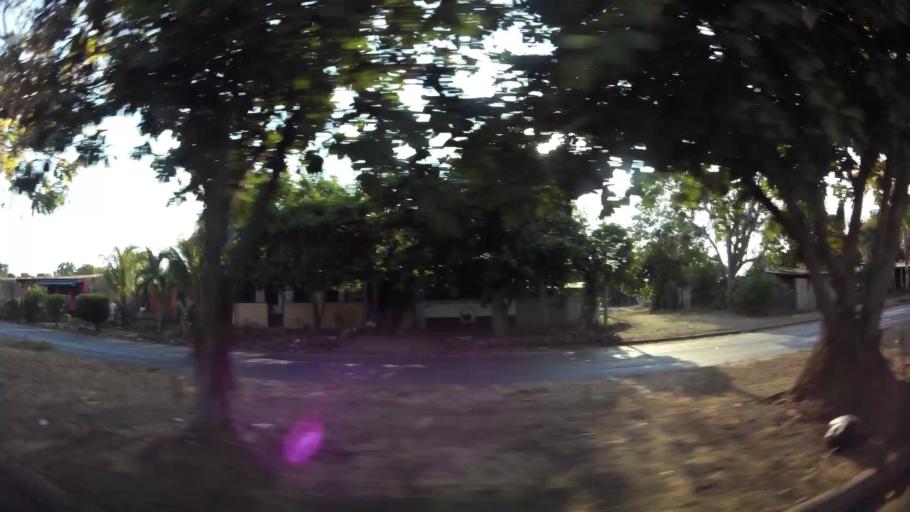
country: NI
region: Managua
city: Managua
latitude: 12.1330
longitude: -86.2750
